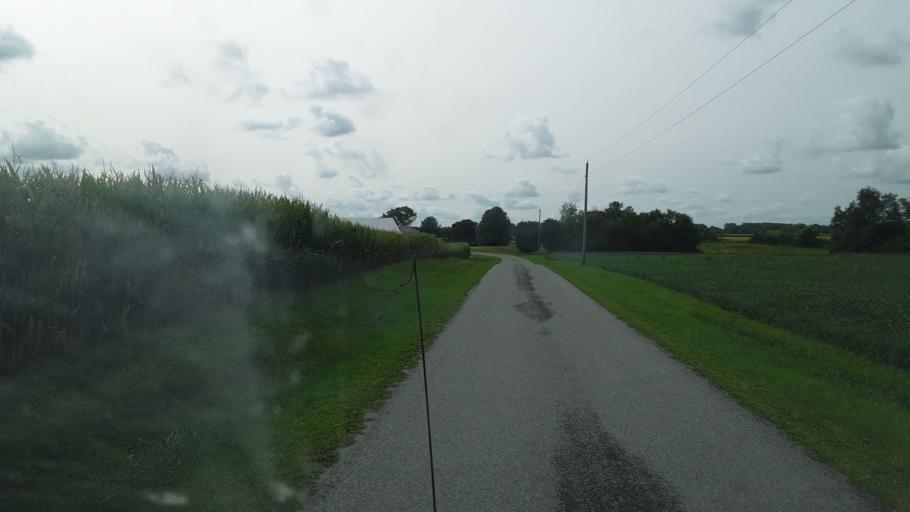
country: US
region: Ohio
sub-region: Crawford County
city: Bucyrus
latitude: 40.6659
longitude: -82.9272
